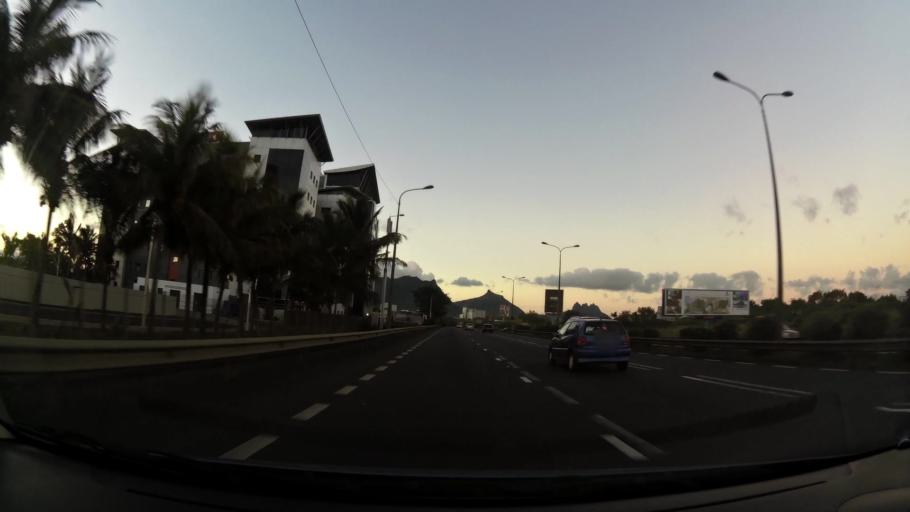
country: MU
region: Plaines Wilhems
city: Ebene
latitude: -20.2448
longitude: 57.4960
